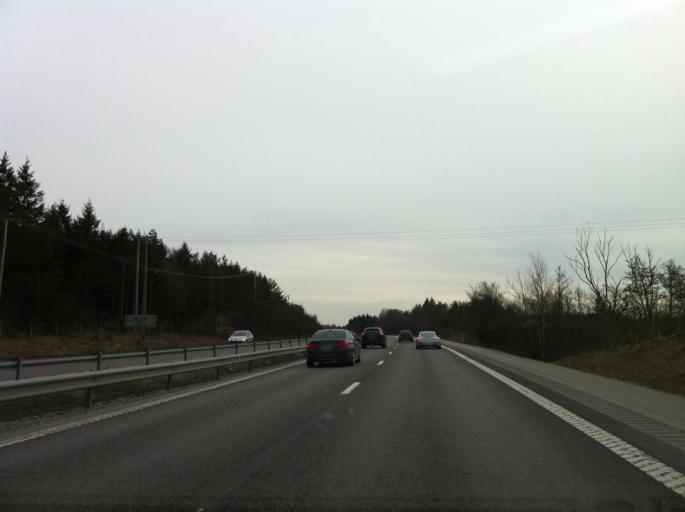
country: SE
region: Vaestra Goetaland
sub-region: Stenungsunds Kommun
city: Stora Hoga
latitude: 58.0029
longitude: 11.8444
